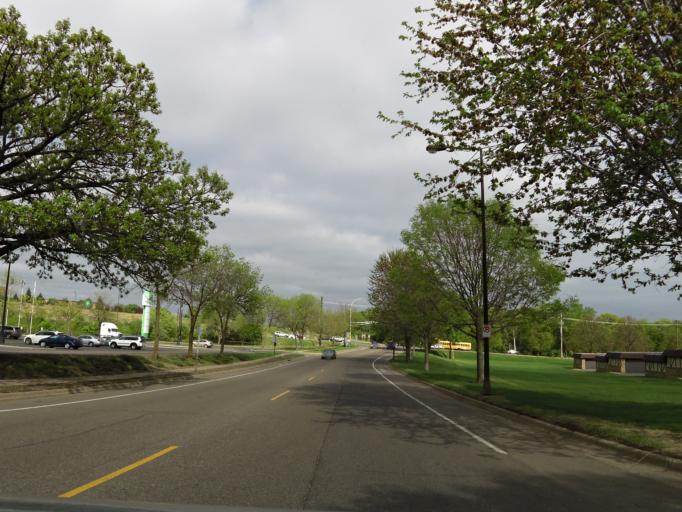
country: US
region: Minnesota
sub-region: Ramsey County
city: Maplewood
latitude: 44.9486
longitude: -93.0069
